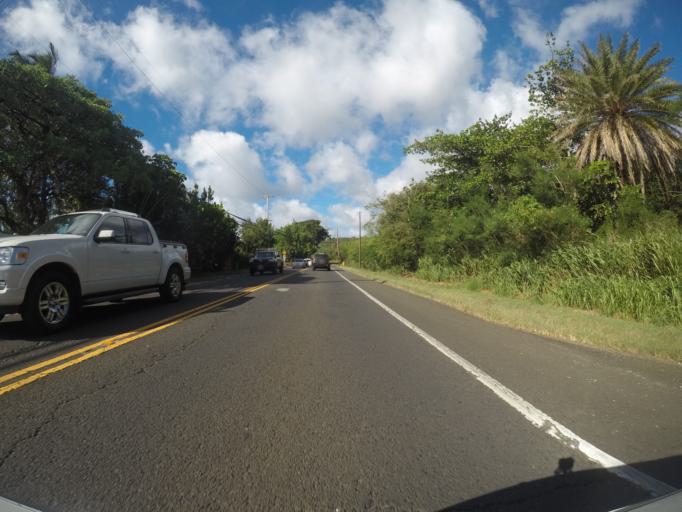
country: US
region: Hawaii
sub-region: Honolulu County
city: Pupukea
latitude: 21.6252
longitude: -158.0764
